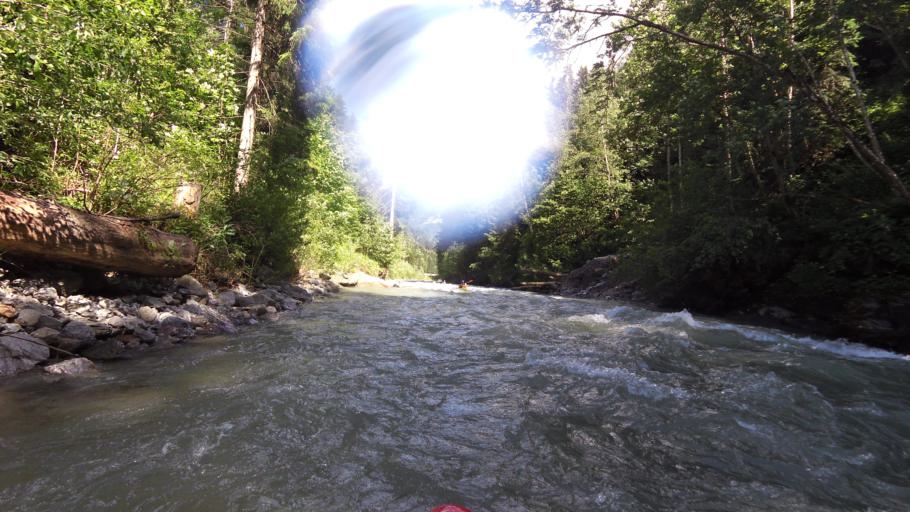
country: AT
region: Tyrol
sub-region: Politischer Bezirk Landeck
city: Strengen
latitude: 47.1224
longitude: 10.4673
